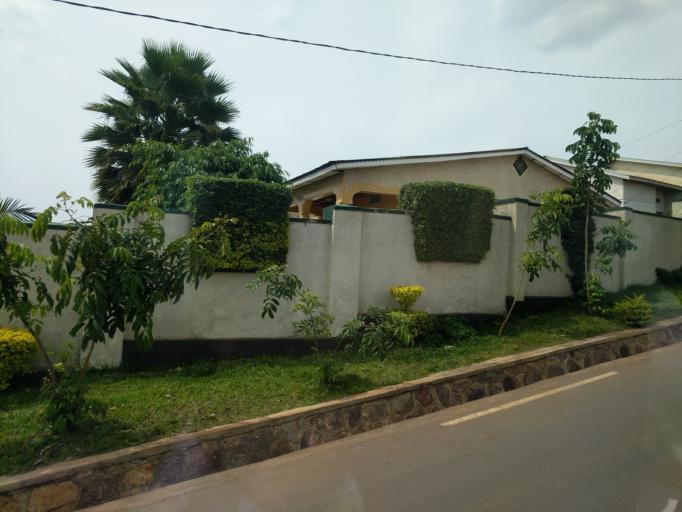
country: RW
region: Kigali
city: Kigali
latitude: -1.9719
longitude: 30.1229
